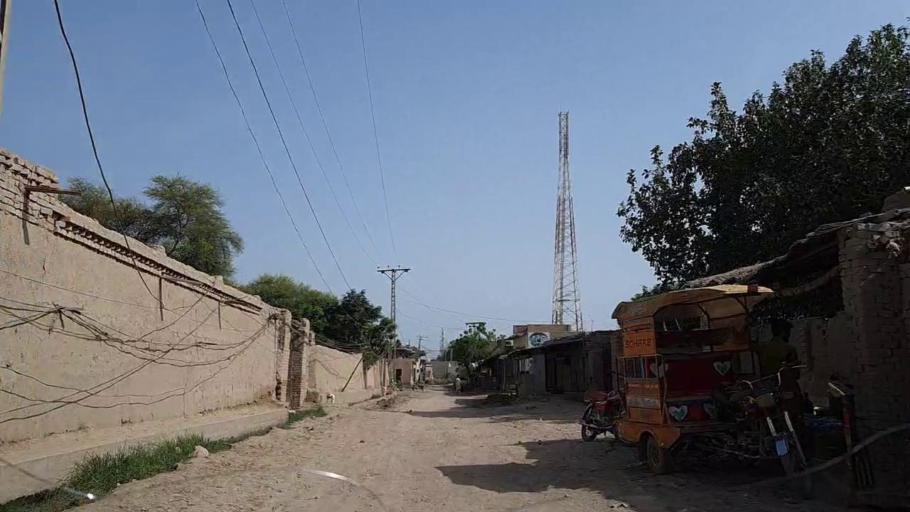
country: PK
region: Sindh
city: Kandiaro
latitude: 27.0646
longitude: 68.2064
